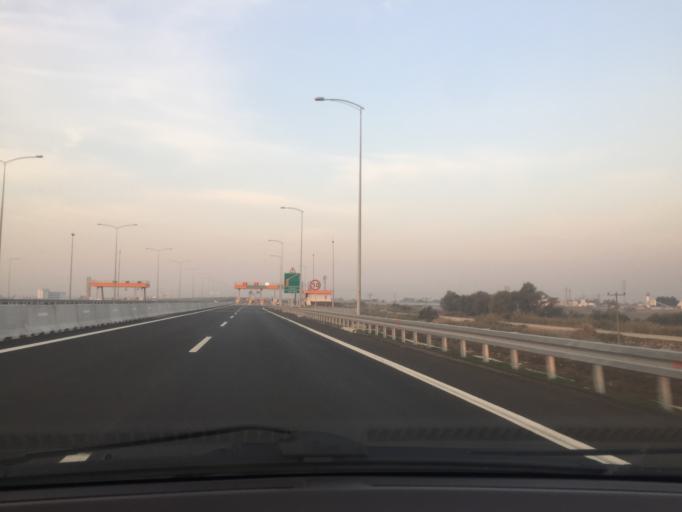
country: TR
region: Bursa
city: Karacabey
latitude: 40.1965
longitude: 28.3639
